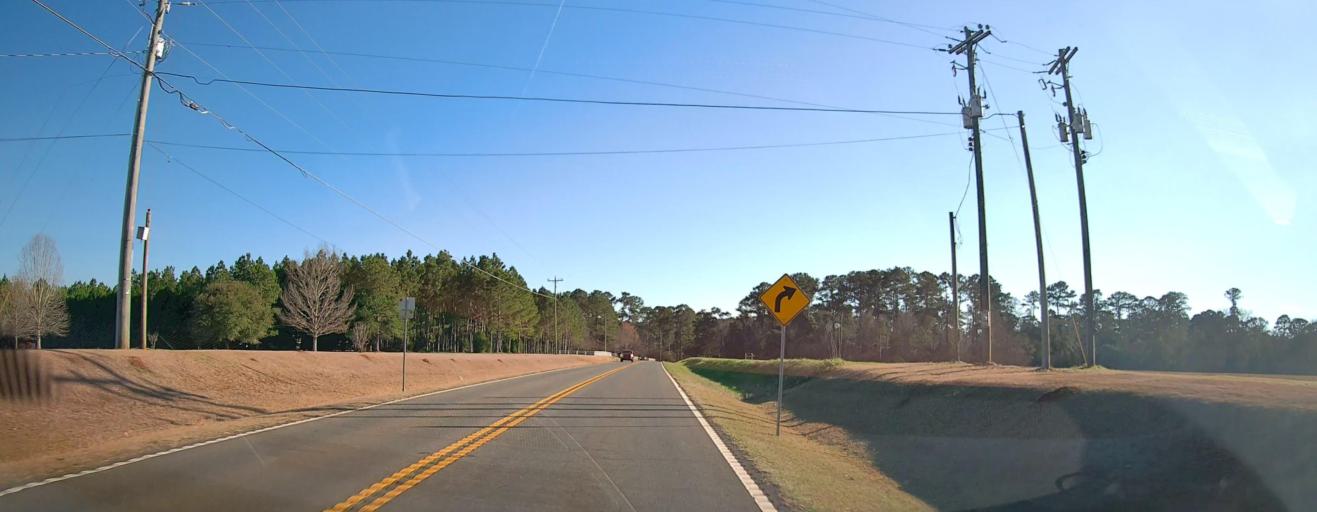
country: US
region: Georgia
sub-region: Sumter County
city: Americus
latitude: 32.0334
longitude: -84.2193
